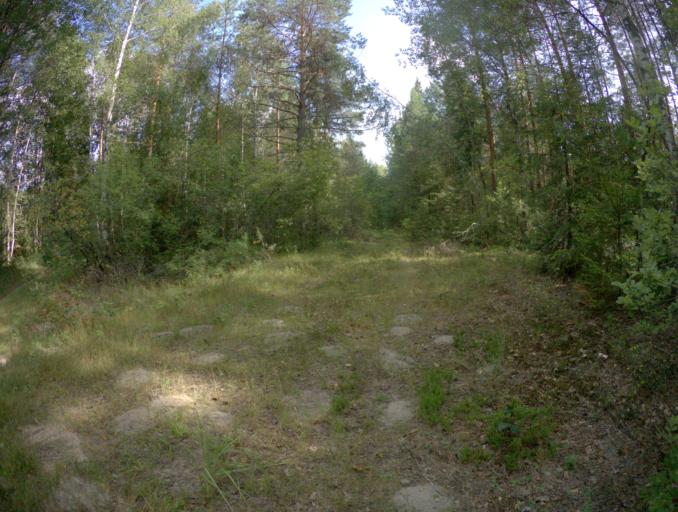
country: RU
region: Vladimir
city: Sobinka
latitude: 55.9206
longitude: 40.0724
